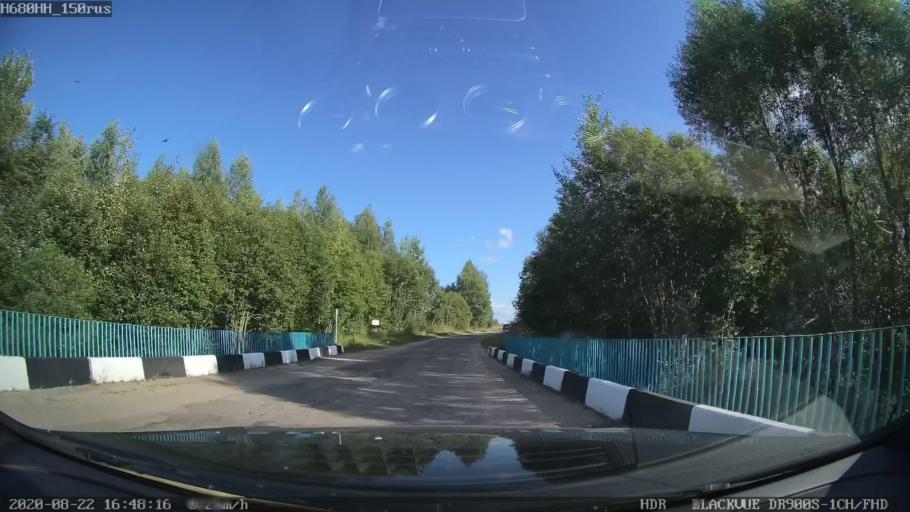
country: RU
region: Tverskaya
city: Rameshki
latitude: 57.2860
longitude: 36.0901
